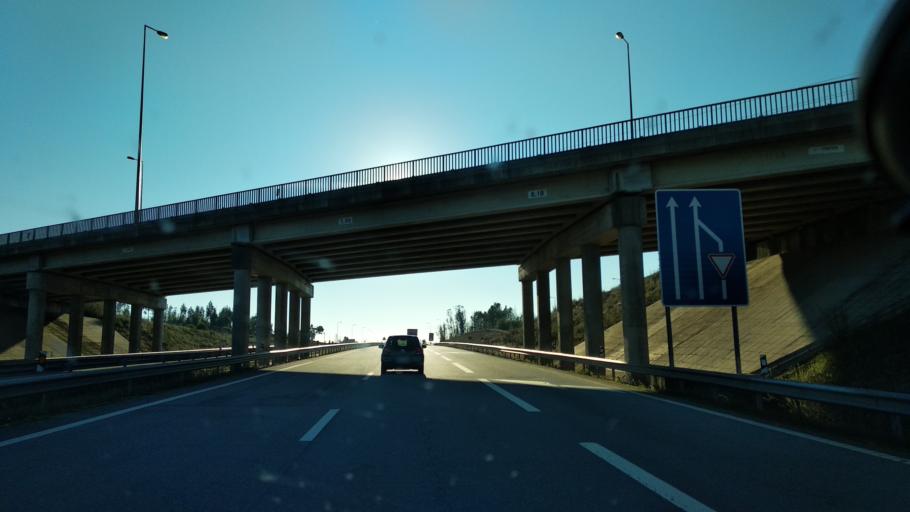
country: PT
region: Santarem
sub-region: Macao
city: Macao
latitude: 39.5144
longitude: -8.0121
